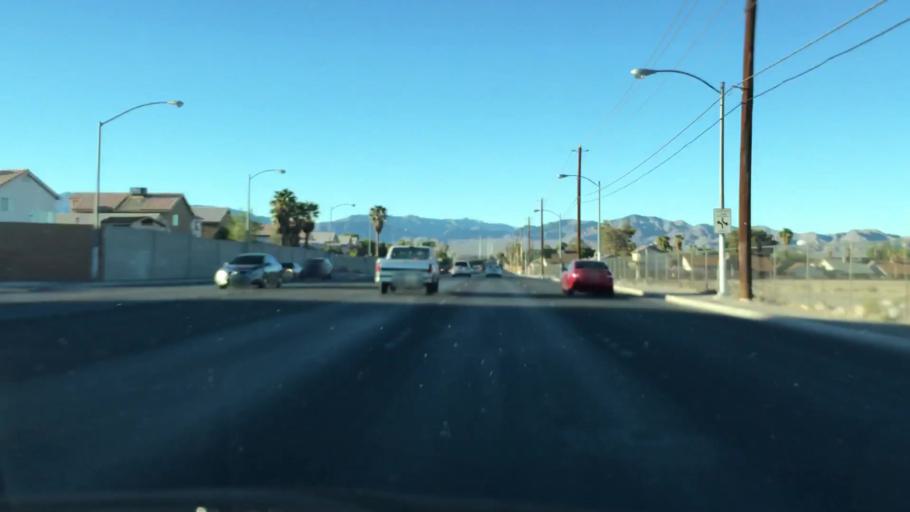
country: US
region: Nevada
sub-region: Clark County
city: Sunrise Manor
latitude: 36.2273
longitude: -115.0801
